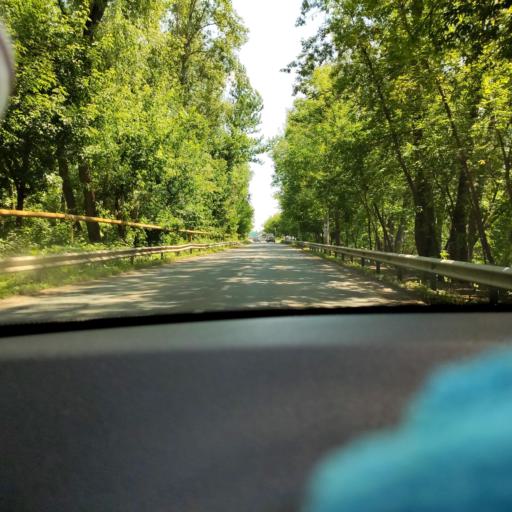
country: RU
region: Samara
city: Novokuybyshevsk
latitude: 53.1489
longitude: 49.9811
